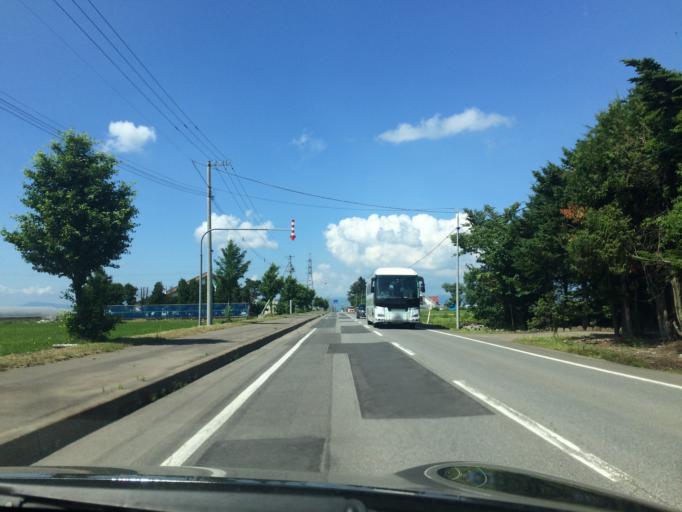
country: JP
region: Hokkaido
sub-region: Asahikawa-shi
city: Asahikawa
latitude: 43.7528
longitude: 142.4624
